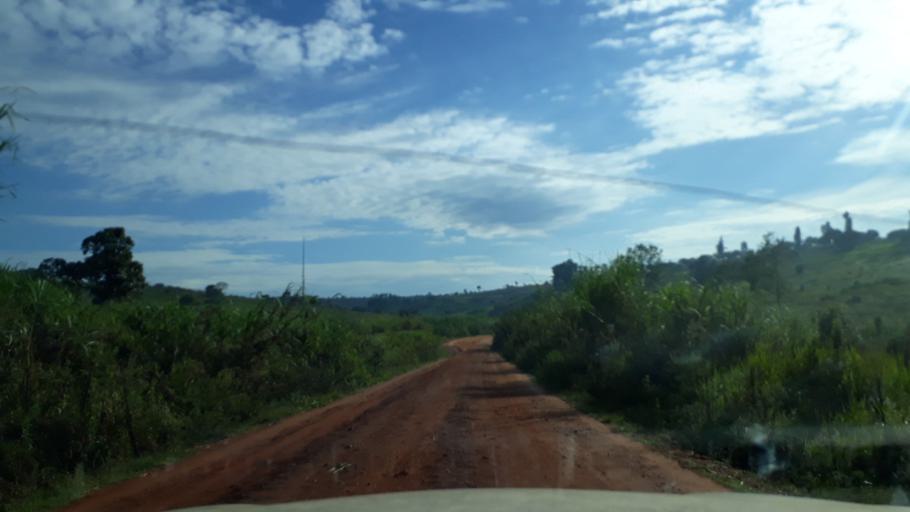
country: UG
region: Northern Region
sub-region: Zombo District
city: Paidha
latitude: 2.2611
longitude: 30.9385
